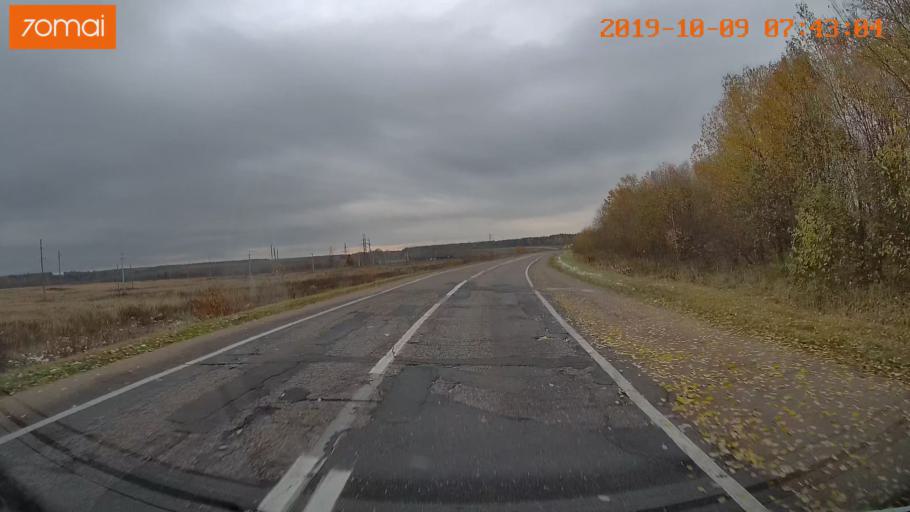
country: RU
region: Jaroslavl
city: Kukoboy
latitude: 58.6449
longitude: 39.7296
